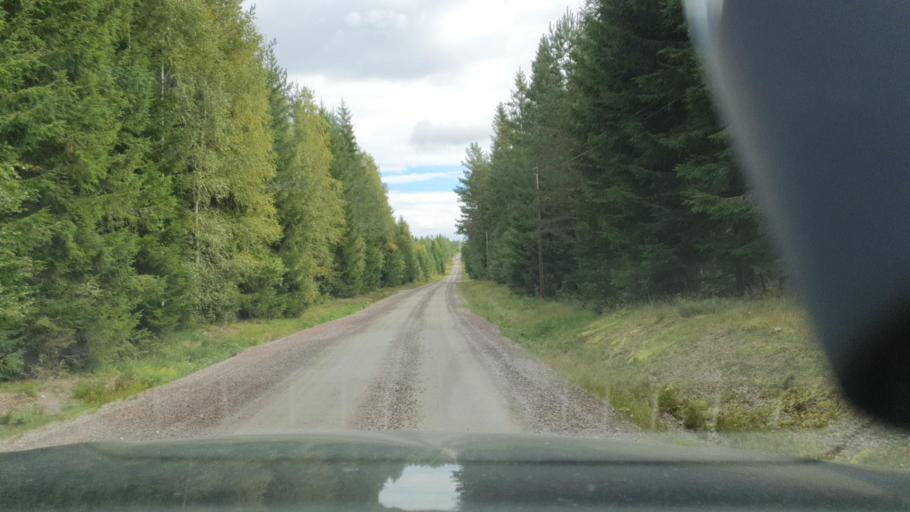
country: SE
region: Vaermland
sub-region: Hagfors Kommun
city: Ekshaerad
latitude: 60.2093
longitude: 13.5815
